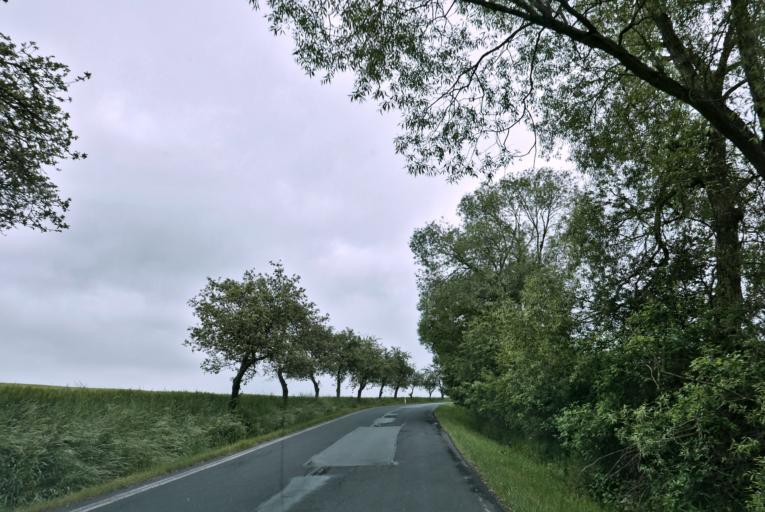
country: CZ
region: Plzensky
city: Plasy
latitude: 49.9841
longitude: 13.4059
